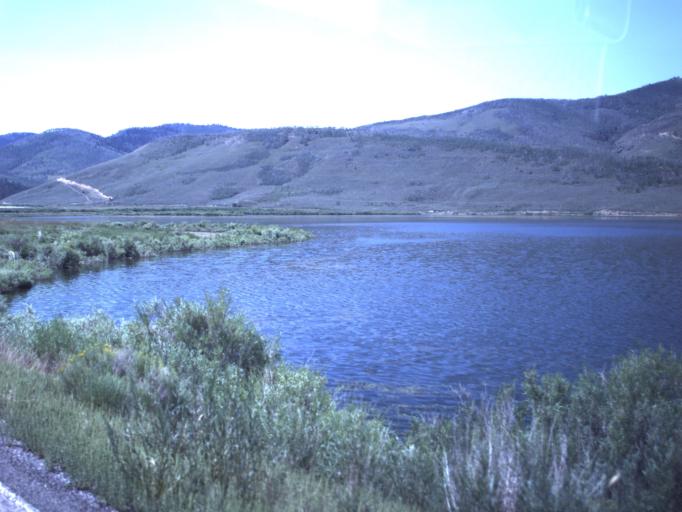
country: US
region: Utah
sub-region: Carbon County
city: Helper
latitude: 39.7524
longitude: -111.1496
